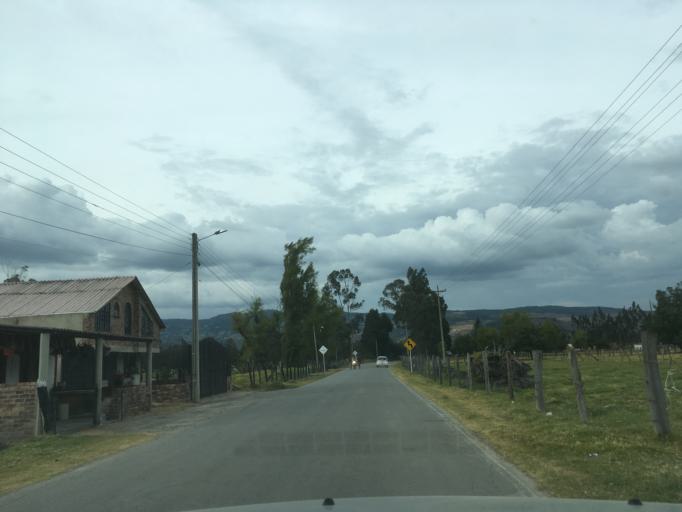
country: CO
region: Boyaca
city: Firavitoba
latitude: 5.6585
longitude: -72.9905
